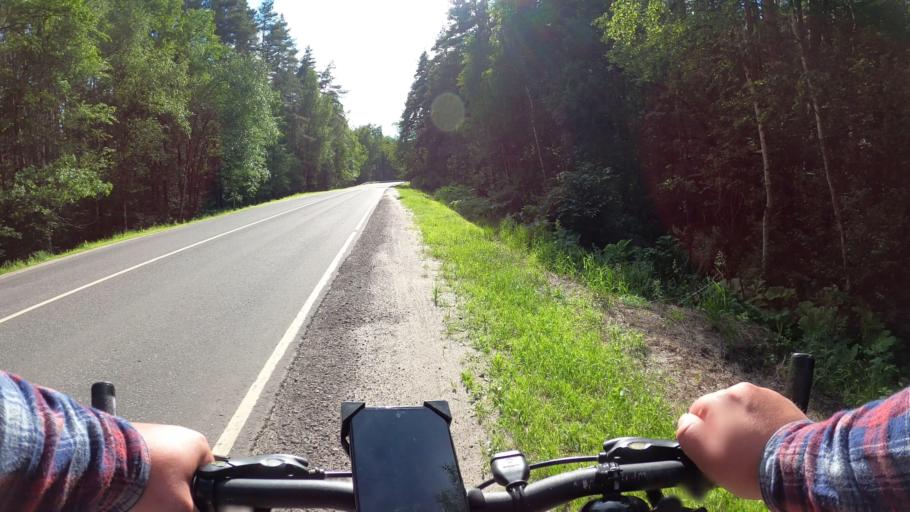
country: RU
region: Moskovskaya
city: Konobeyevo
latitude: 55.4349
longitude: 38.6517
